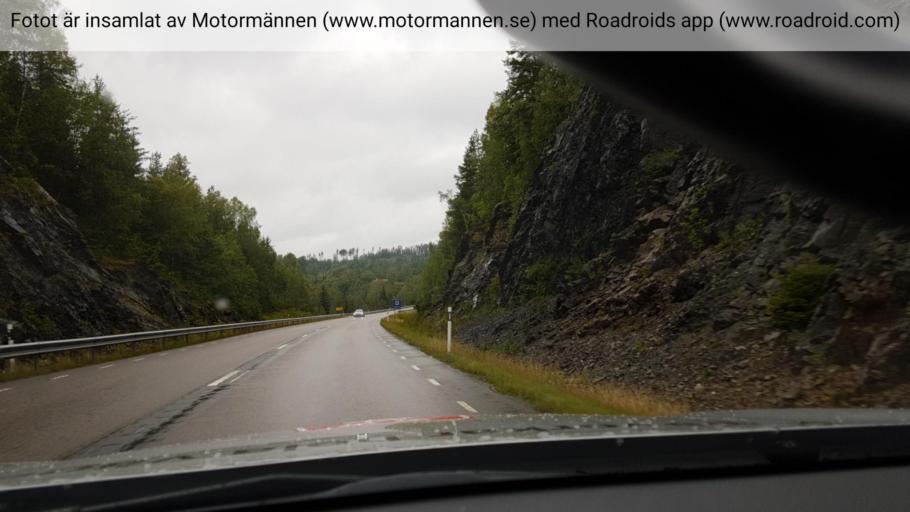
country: SE
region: Vaestra Goetaland
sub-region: Bengtsfors Kommun
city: Billingsfors
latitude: 58.9277
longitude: 12.1421
